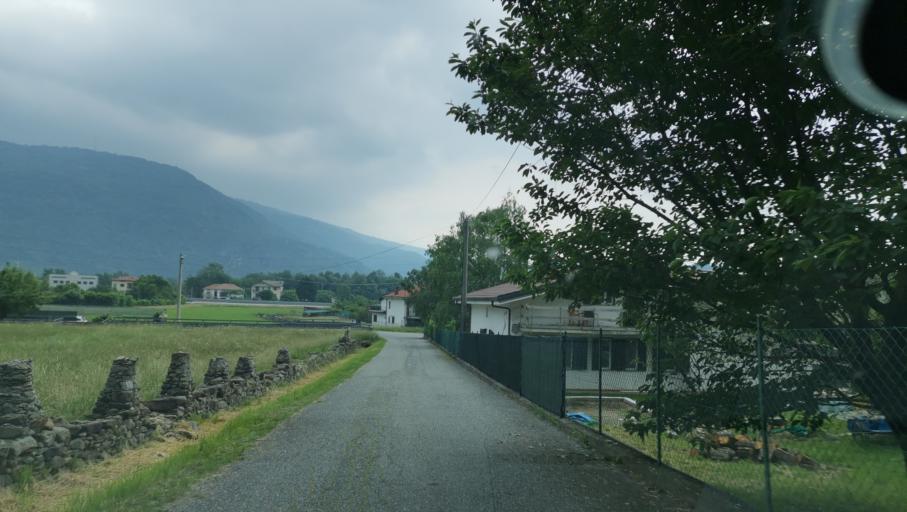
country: IT
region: Piedmont
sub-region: Provincia di Torino
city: Quassolo
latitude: 45.5212
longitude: 7.8314
